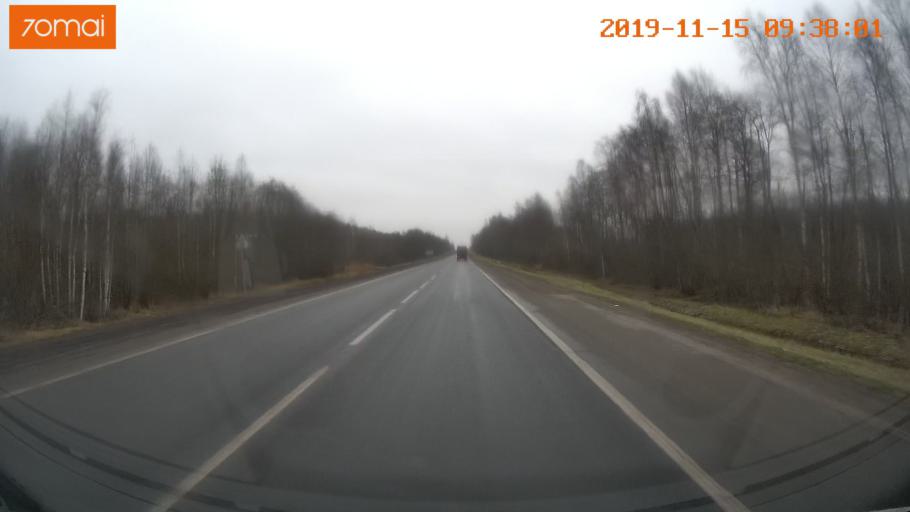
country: RU
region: Vologda
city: Sheksna
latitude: 59.2357
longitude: 38.4476
